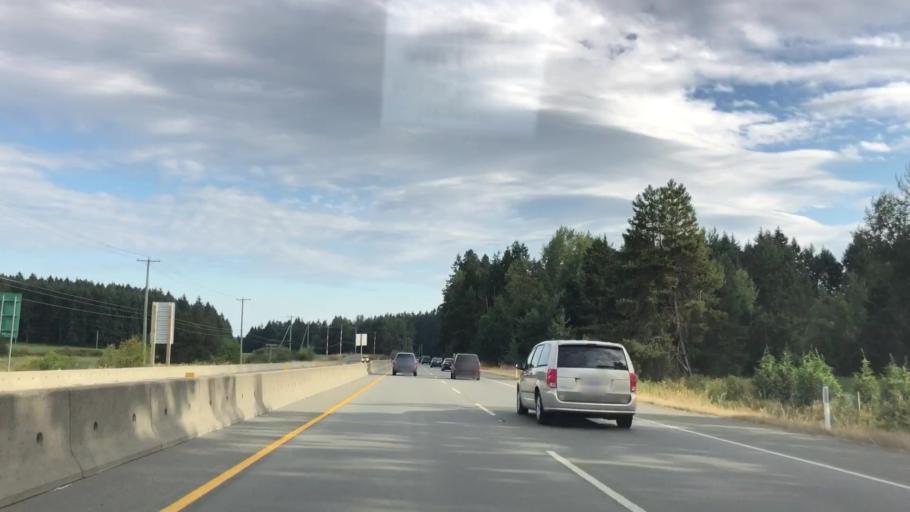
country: CA
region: British Columbia
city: Duncan
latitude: 48.7270
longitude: -123.6380
